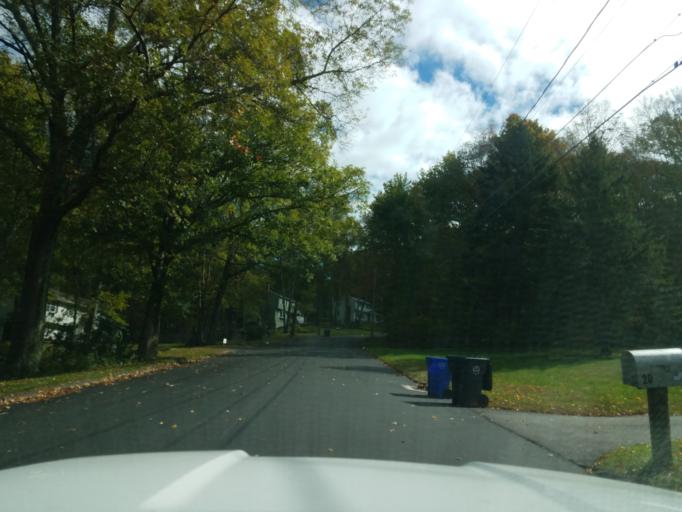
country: US
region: Connecticut
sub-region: Tolland County
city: South Coventry
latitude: 41.7161
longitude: -72.2758
